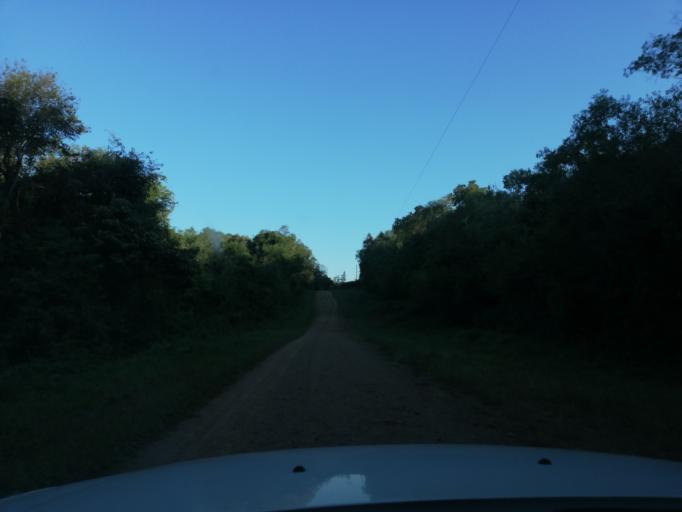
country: AR
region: Misiones
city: Cerro Cora
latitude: -27.6156
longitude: -55.7062
